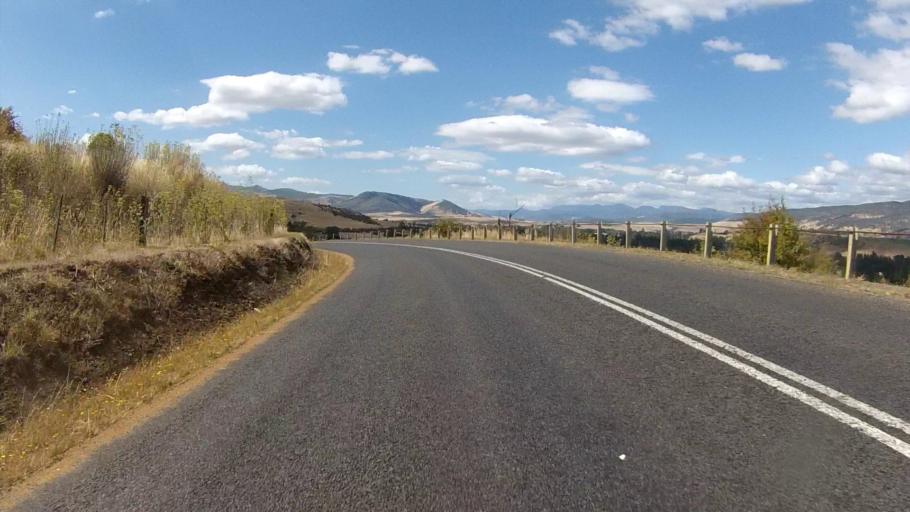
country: AU
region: Tasmania
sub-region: Derwent Valley
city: New Norfolk
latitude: -42.6903
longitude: 146.8782
